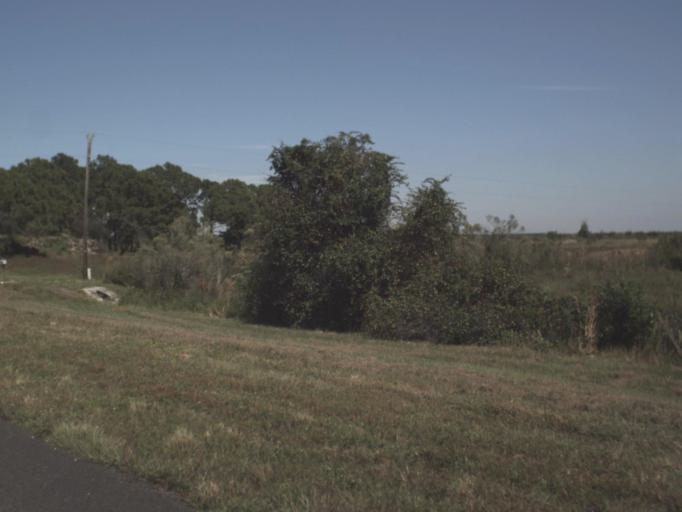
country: US
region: Florida
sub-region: Highlands County
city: Placid Lakes
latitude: 27.1054
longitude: -81.3322
